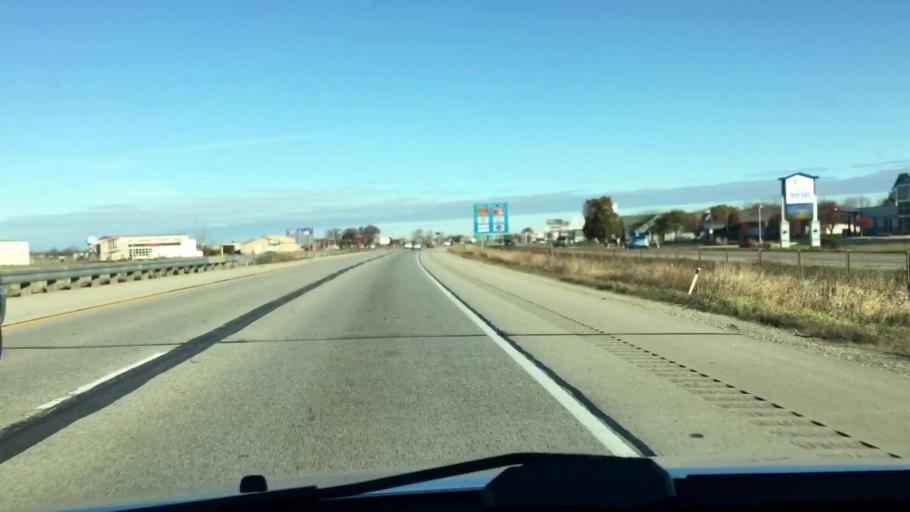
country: US
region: Wisconsin
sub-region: Fond du Lac County
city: North Fond du Lac
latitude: 43.7711
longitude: -88.4817
